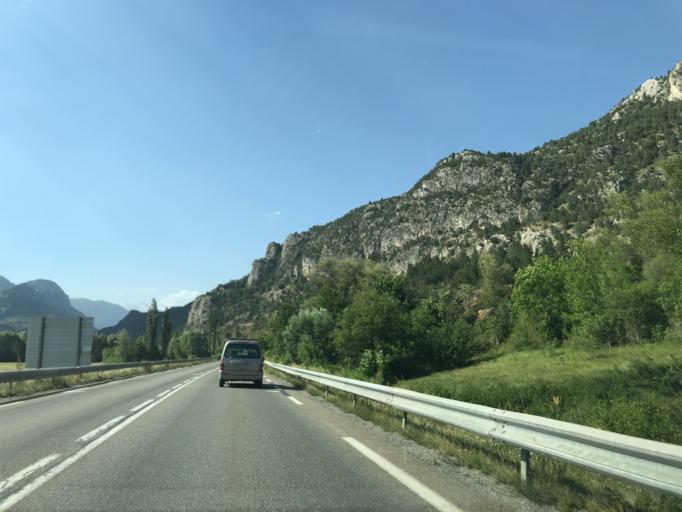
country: FR
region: Provence-Alpes-Cote d'Azur
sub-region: Departement des Hautes-Alpes
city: Guillestre
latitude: 44.7084
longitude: 6.6035
